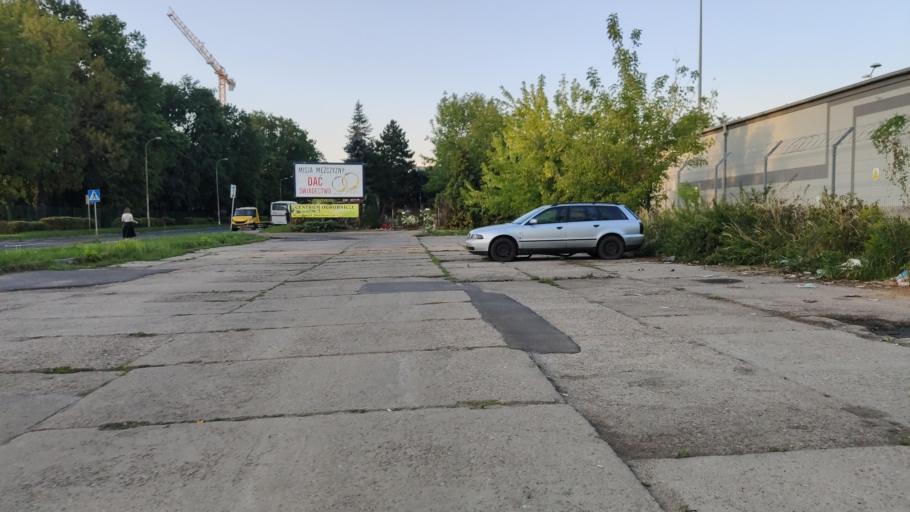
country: PL
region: Lower Silesian Voivodeship
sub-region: Powiat wroclawski
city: Wroclaw
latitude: 51.0783
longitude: 16.9985
